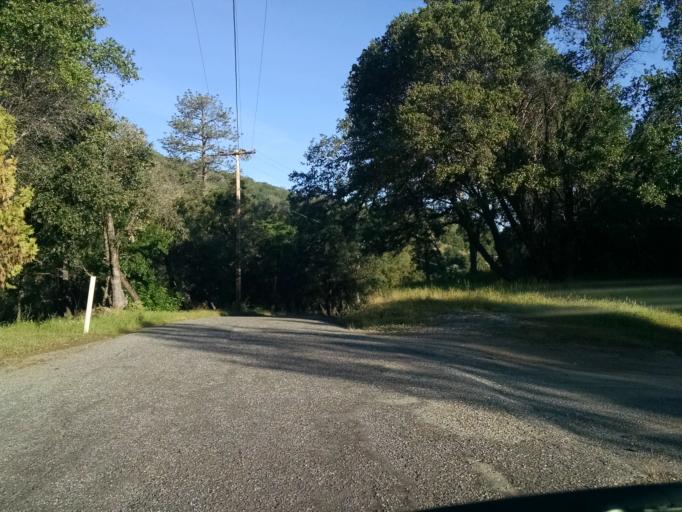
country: US
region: California
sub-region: Madera County
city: Oakhurst
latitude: 37.3077
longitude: -119.6508
